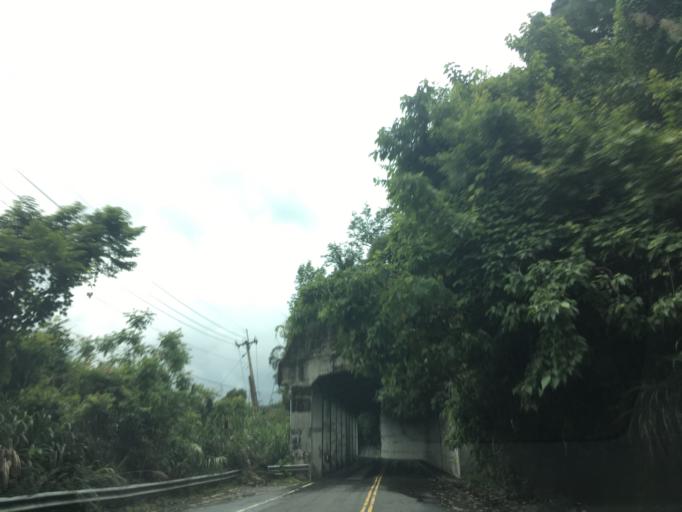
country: TW
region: Taiwan
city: Lugu
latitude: 23.5328
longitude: 120.7038
